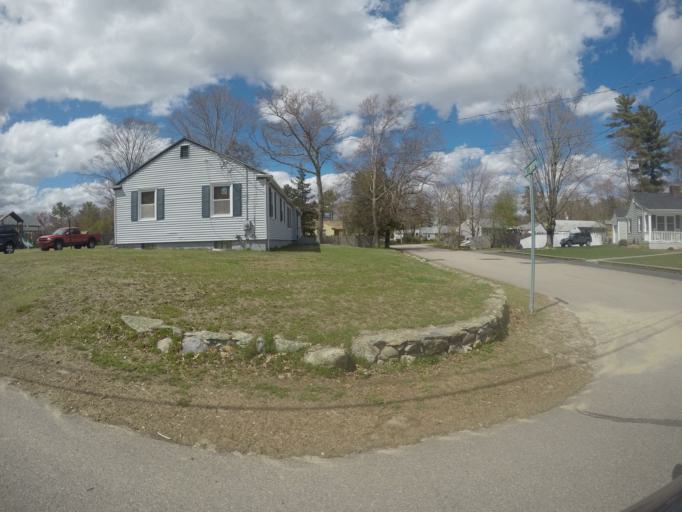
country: US
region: Massachusetts
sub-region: Bristol County
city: Easton
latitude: 42.0299
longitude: -71.0726
